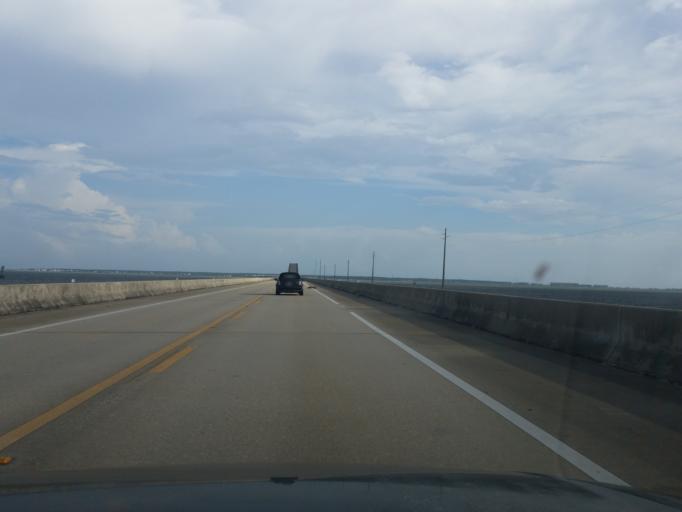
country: US
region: Alabama
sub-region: Mobile County
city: Dauphin Island
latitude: 30.3005
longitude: -88.1347
